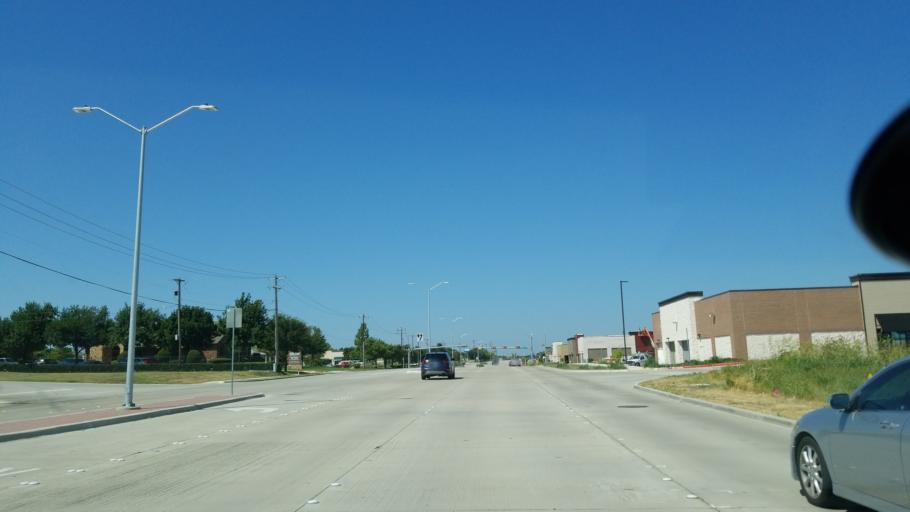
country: US
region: Texas
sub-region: Tarrant County
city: Mansfield
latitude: 32.5710
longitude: -97.1106
